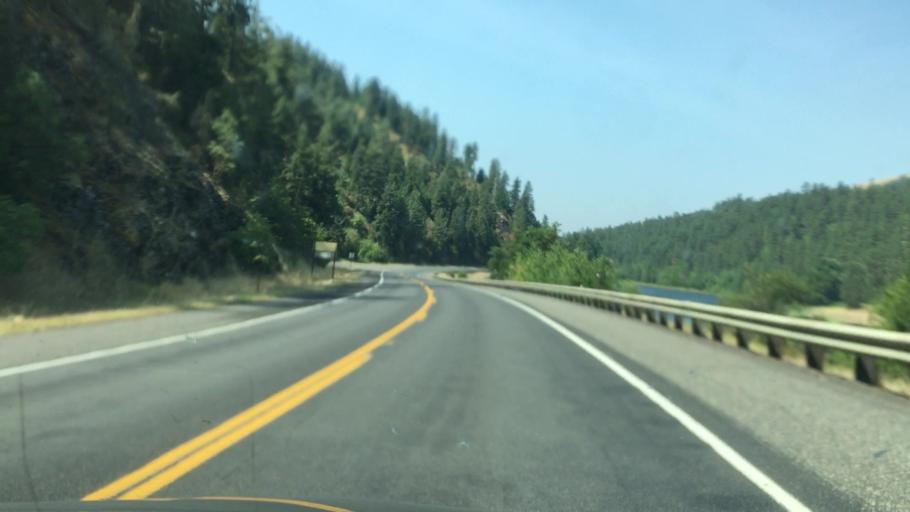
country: US
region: Idaho
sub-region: Clearwater County
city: Orofino
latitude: 46.5023
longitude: -116.3523
